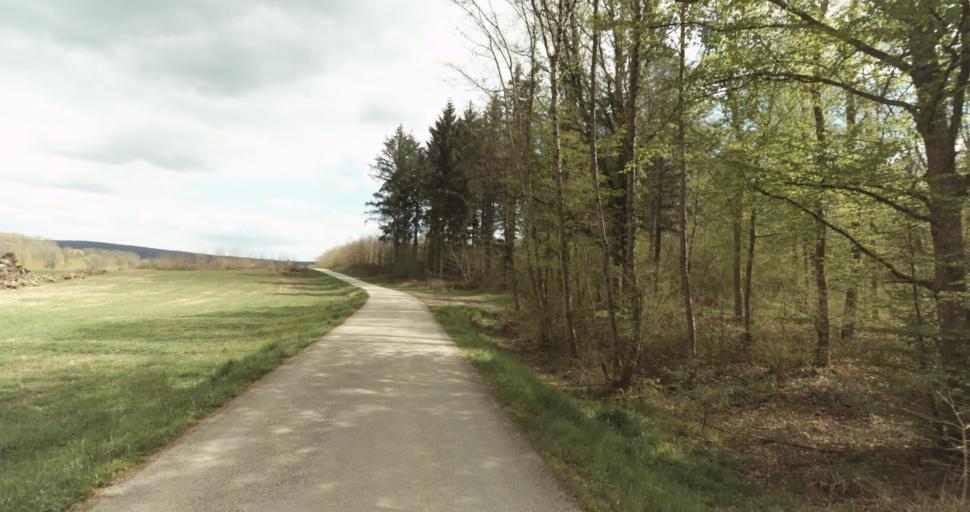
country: FR
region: Bourgogne
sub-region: Departement de la Cote-d'Or
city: Auxonne
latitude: 47.1807
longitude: 5.4578
